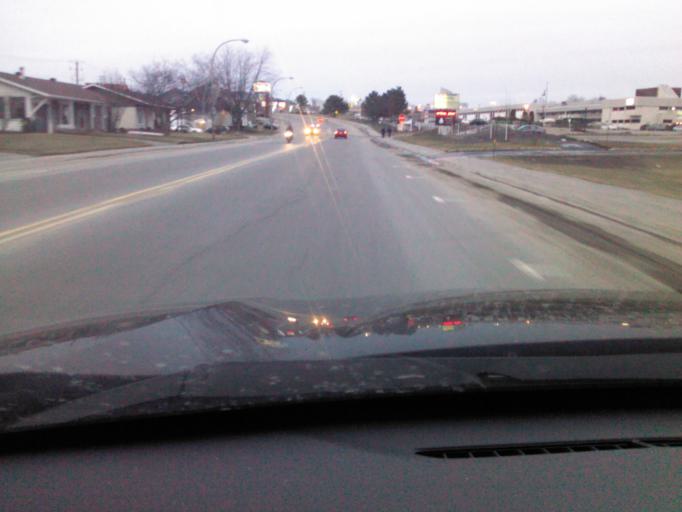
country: CA
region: Quebec
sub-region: Capitale-Nationale
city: Donnacona
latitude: 46.6790
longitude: -71.7317
